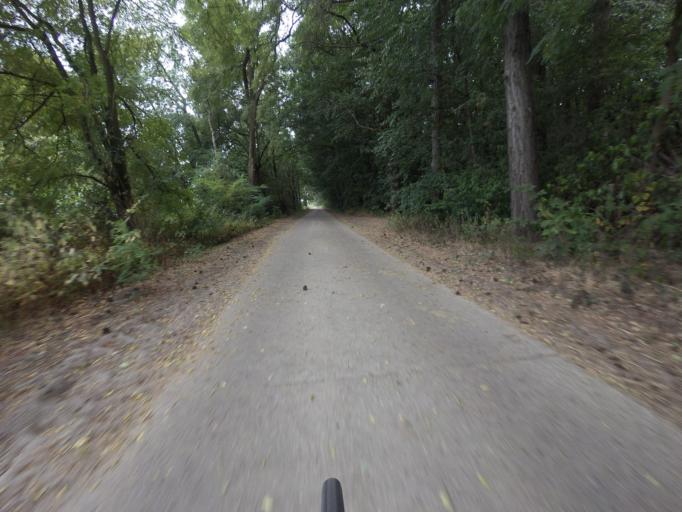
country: BE
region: Flanders
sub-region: Provincie Antwerpen
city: Brecht
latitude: 51.3143
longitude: 4.6112
